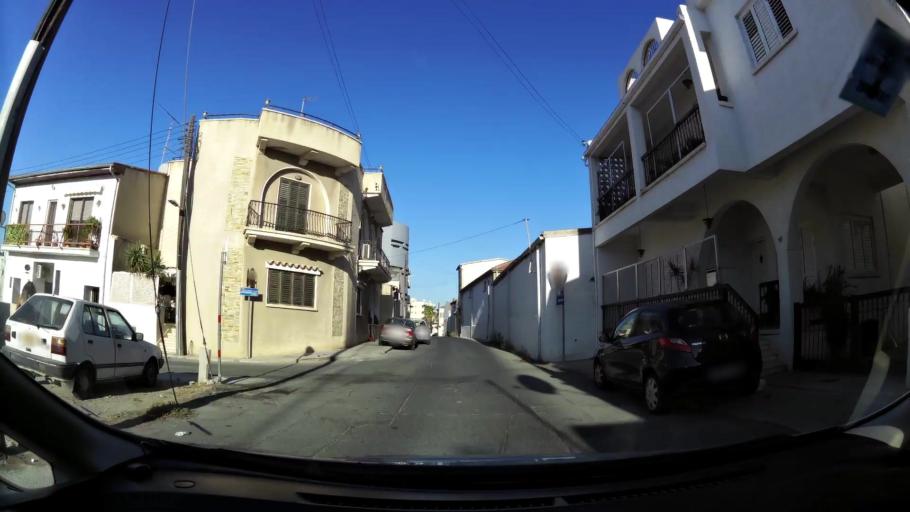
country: CY
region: Larnaka
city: Larnaca
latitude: 34.9212
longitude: 33.6301
